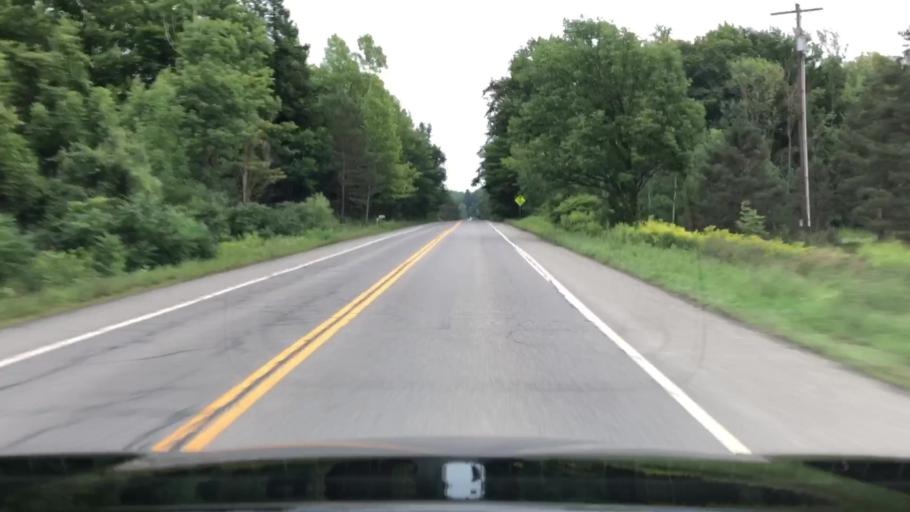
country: US
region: New York
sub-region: Erie County
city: Orchard Park
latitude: 42.7602
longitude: -78.6969
